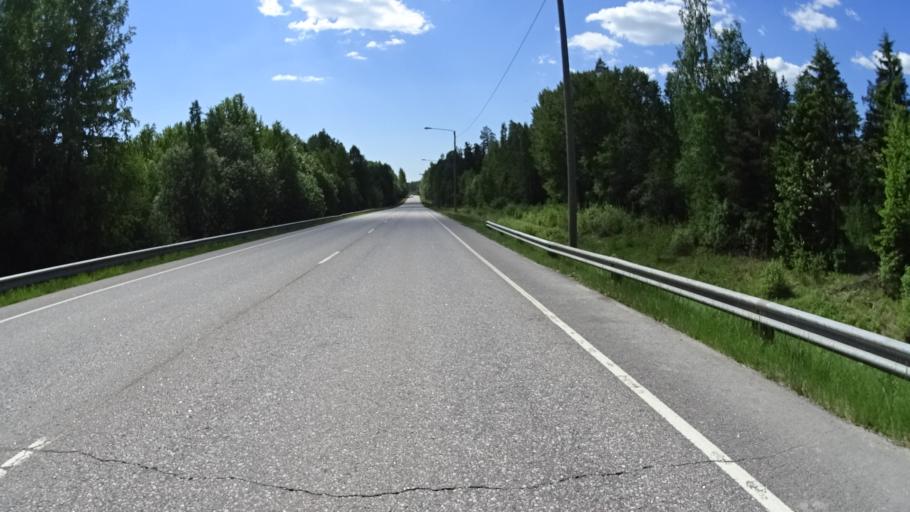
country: FI
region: Uusimaa
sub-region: Helsinki
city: Nurmijaervi
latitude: 60.3802
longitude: 24.8069
